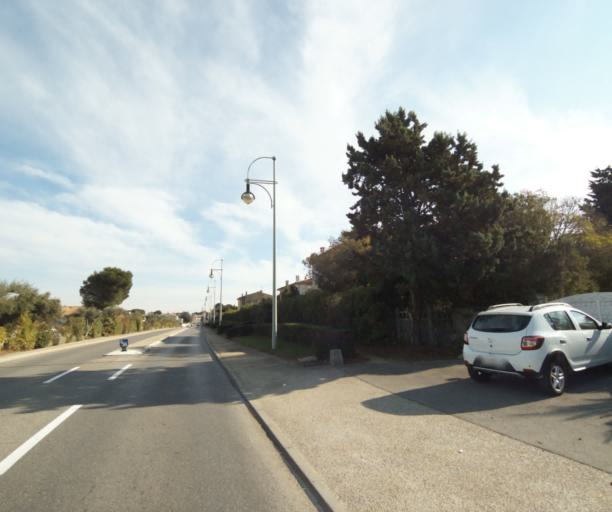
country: FR
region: Provence-Alpes-Cote d'Azur
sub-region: Departement des Bouches-du-Rhone
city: Chateauneuf-les-Martigues
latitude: 43.3972
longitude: 5.1141
